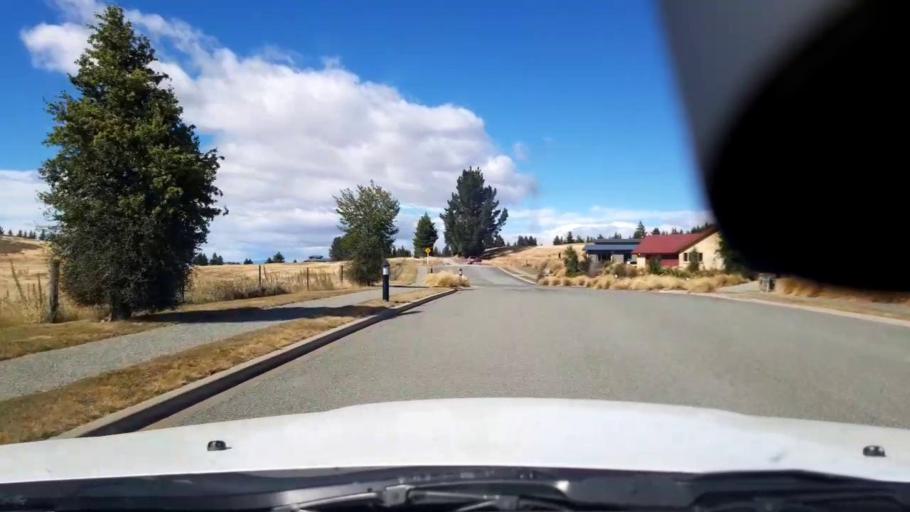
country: NZ
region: Canterbury
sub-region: Timaru District
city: Pleasant Point
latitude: -44.0079
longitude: 170.4741
